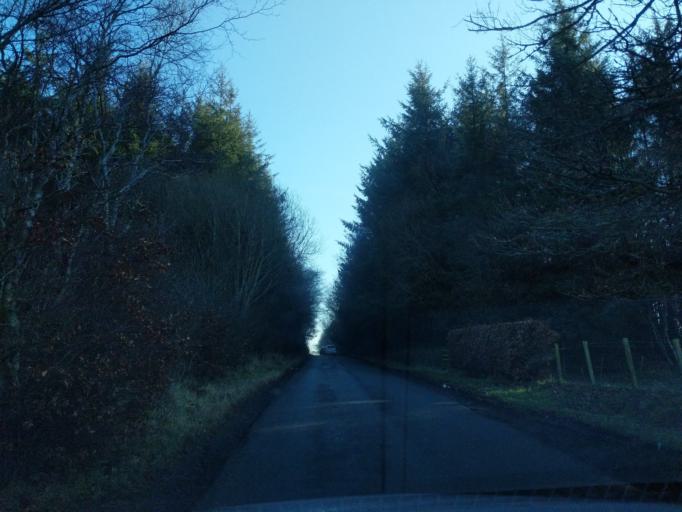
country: GB
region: Scotland
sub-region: South Lanarkshire
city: Carluke
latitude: 55.6931
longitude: -3.8436
